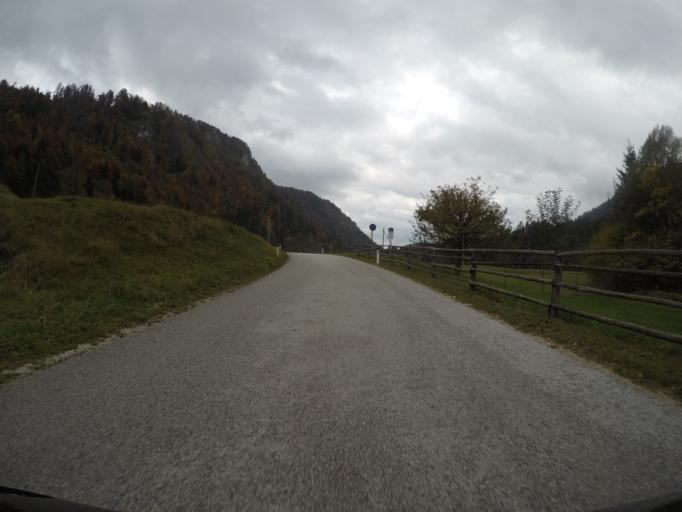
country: SI
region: Gorje
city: Zgornje Gorje
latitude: 46.3843
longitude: 14.0400
